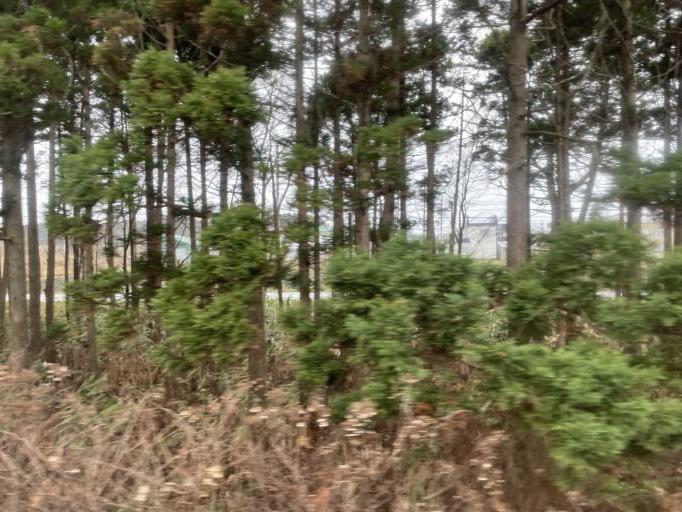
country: JP
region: Aomori
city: Aomori Shi
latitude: 40.9856
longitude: 140.6530
